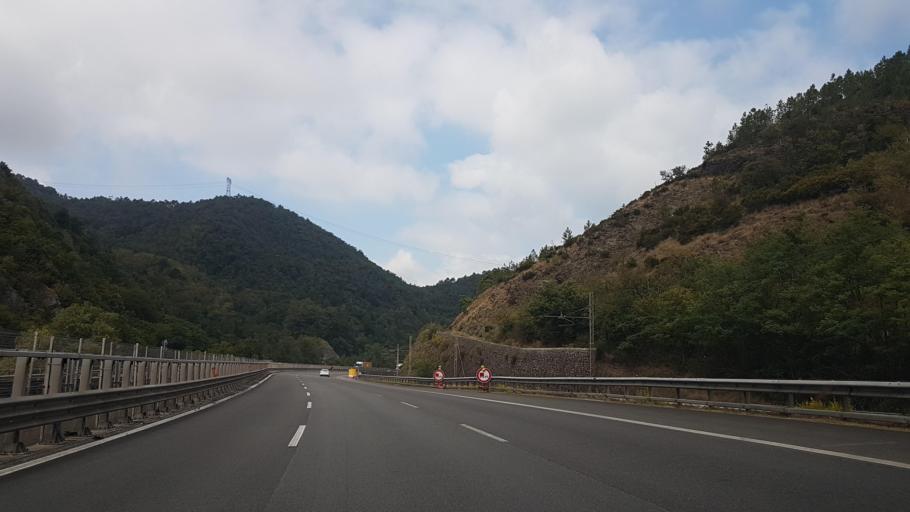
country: IT
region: Piedmont
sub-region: Provincia di Alessandria
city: Belforte Monferrato
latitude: 44.6016
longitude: 8.6660
